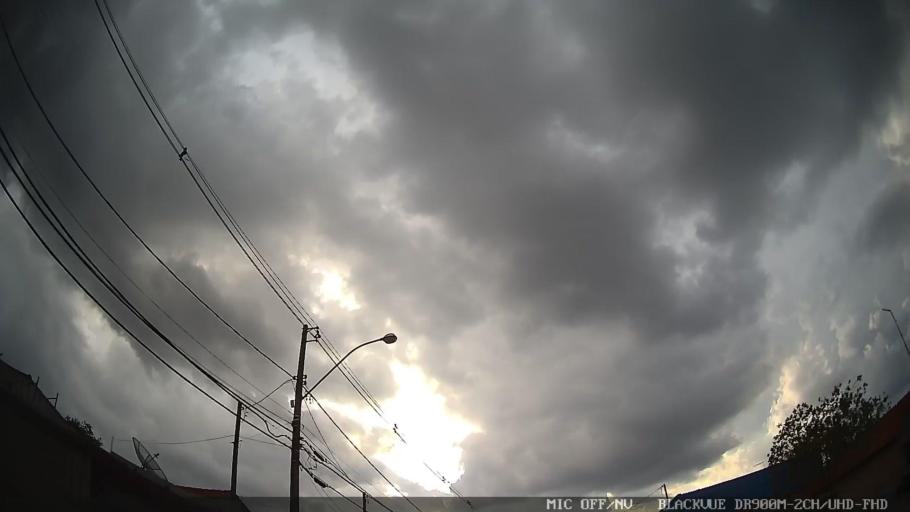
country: BR
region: Sao Paulo
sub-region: Braganca Paulista
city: Braganca Paulista
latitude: -22.9116
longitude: -46.5340
